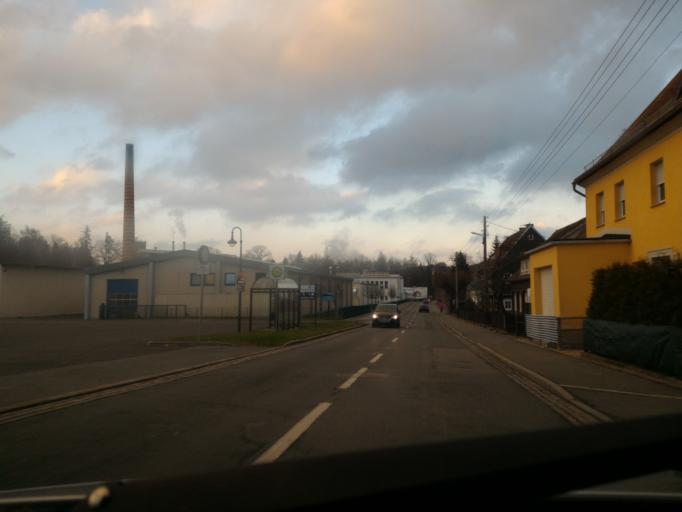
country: DE
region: Saxony
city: Grossschonau
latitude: 50.8929
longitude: 14.6602
